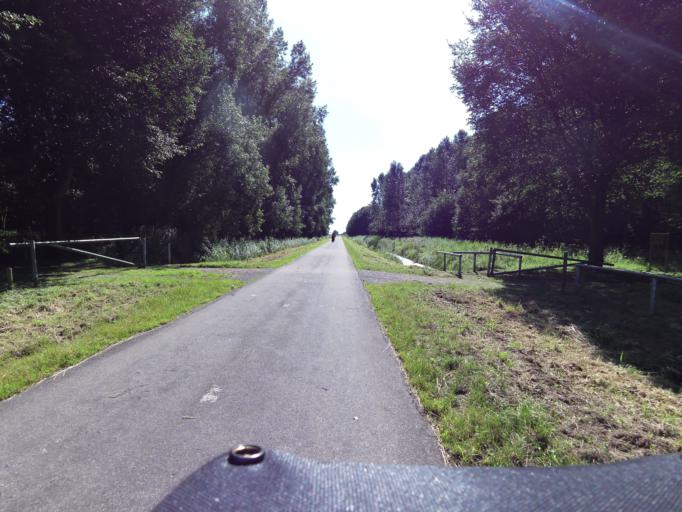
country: NL
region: South Holland
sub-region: Gemeente Spijkenisse
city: Spijkenisse
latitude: 51.8452
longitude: 4.3043
